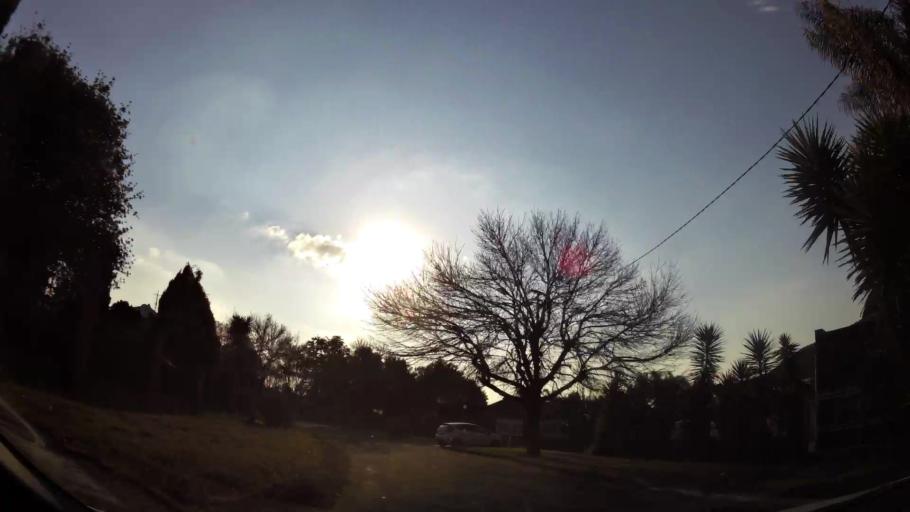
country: ZA
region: Gauteng
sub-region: Ekurhuleni Metropolitan Municipality
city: Springs
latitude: -26.2618
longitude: 28.3894
